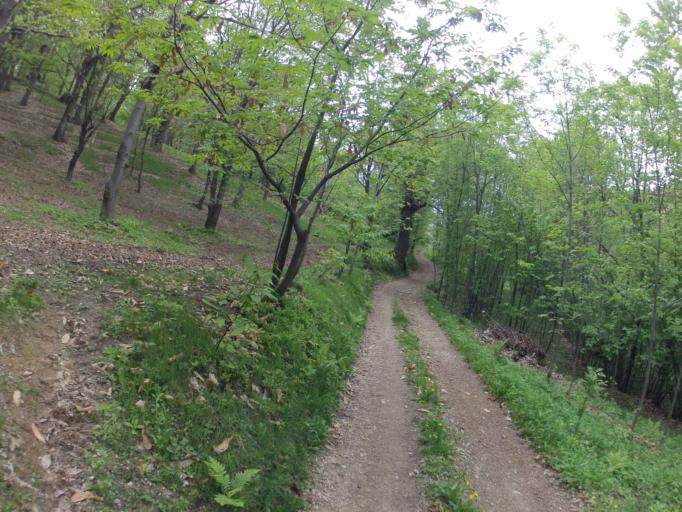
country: IT
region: Piedmont
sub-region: Provincia di Cuneo
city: Peveragno
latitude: 44.3169
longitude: 7.5855
